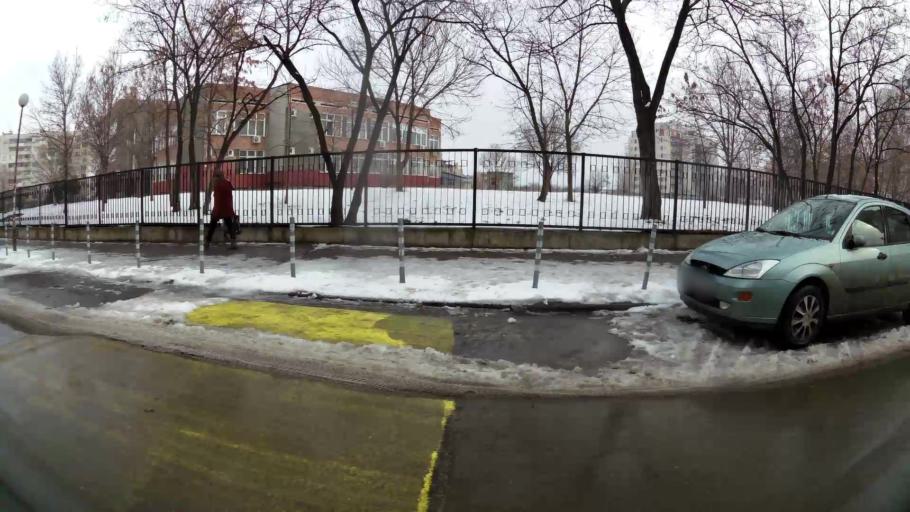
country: BG
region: Sofia-Capital
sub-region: Stolichna Obshtina
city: Sofia
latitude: 42.7130
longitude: 23.3781
